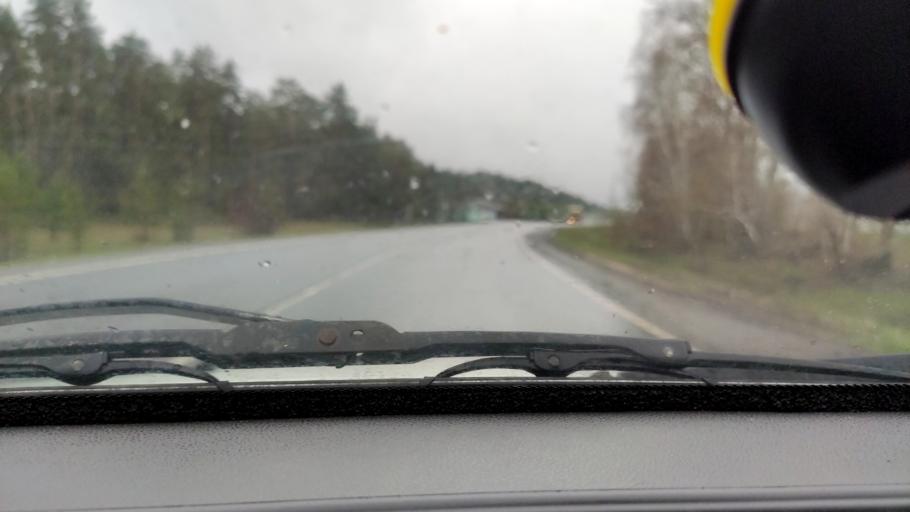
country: RU
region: Samara
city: Povolzhskiy
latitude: 53.6300
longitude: 49.6584
